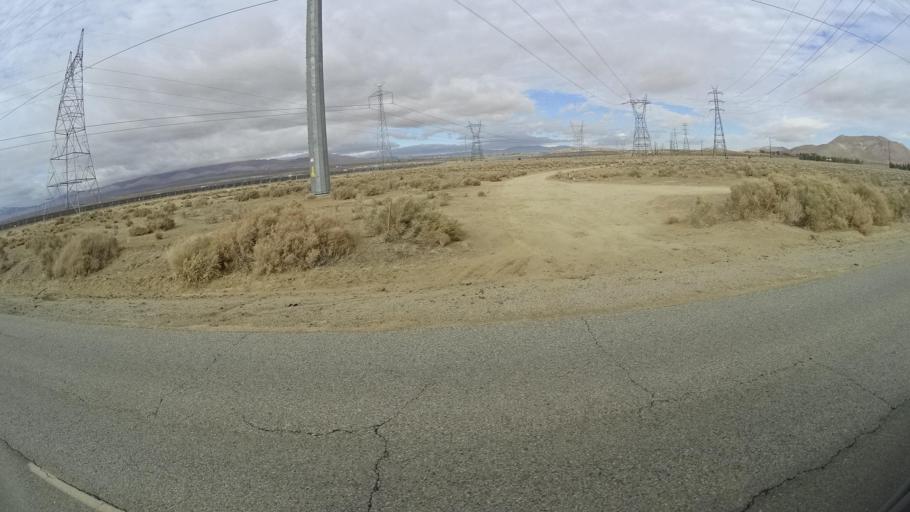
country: US
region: California
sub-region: Kern County
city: Rosamond
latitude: 34.8634
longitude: -118.3147
